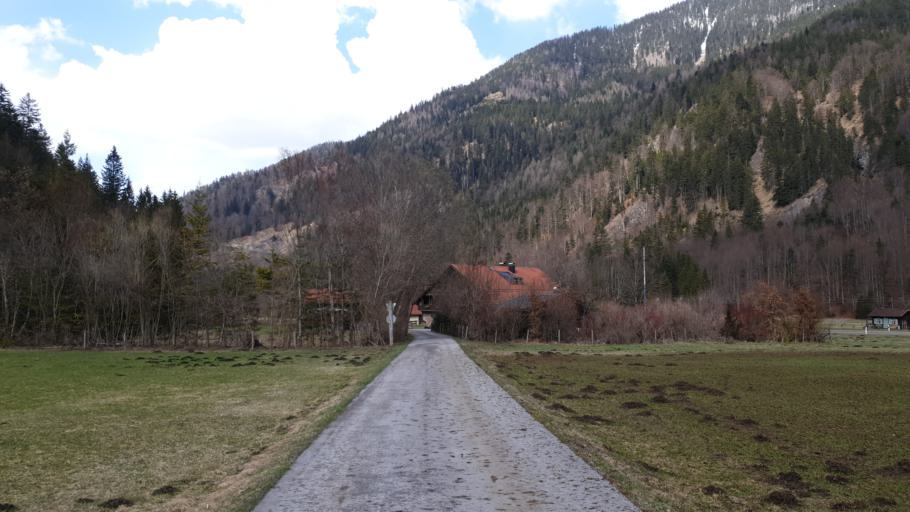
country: DE
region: Bavaria
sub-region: Upper Bavaria
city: Bayrischzell
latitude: 47.6335
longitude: 12.0115
